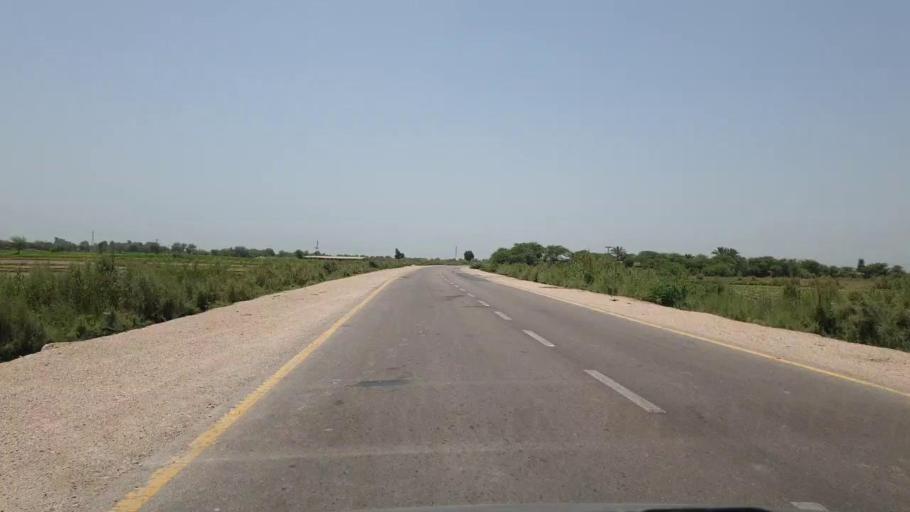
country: PK
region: Sindh
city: Sakrand
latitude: 26.1245
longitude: 68.3817
